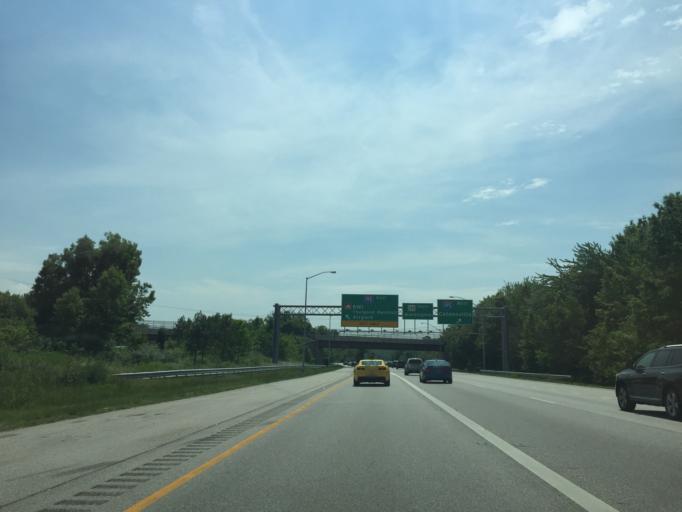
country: US
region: Maryland
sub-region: Howard County
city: Elkridge
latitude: 39.2062
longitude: -76.6886
